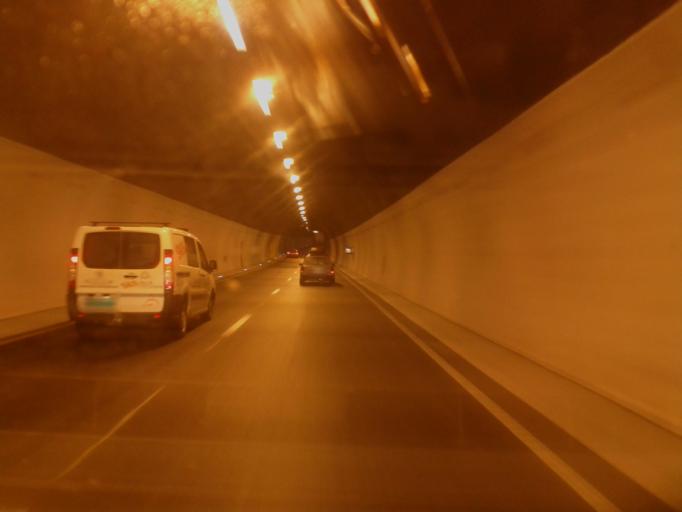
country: NO
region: Sor-Trondelag
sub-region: Trondheim
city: Trondheim
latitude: 63.4275
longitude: 10.5094
